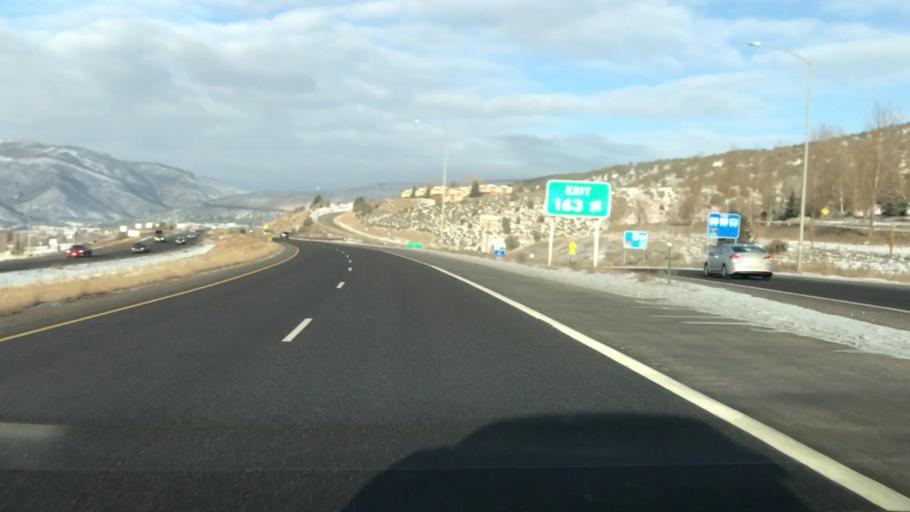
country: US
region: Colorado
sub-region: Eagle County
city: Edwards
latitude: 39.6486
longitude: -106.5844
